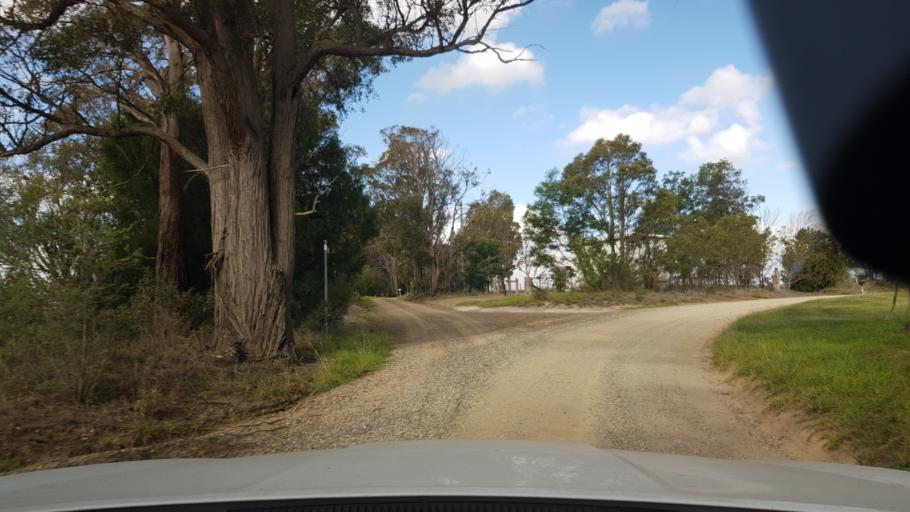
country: AU
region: Victoria
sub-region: East Gippsland
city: Bairnsdale
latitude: -37.7837
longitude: 147.5766
